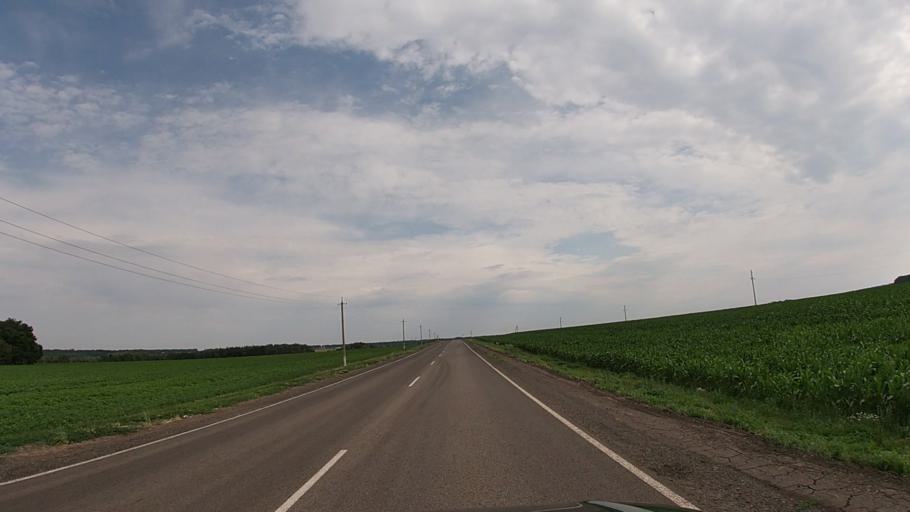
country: RU
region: Belgorod
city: Krasnaya Yaruga
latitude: 50.8163
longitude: 35.5019
